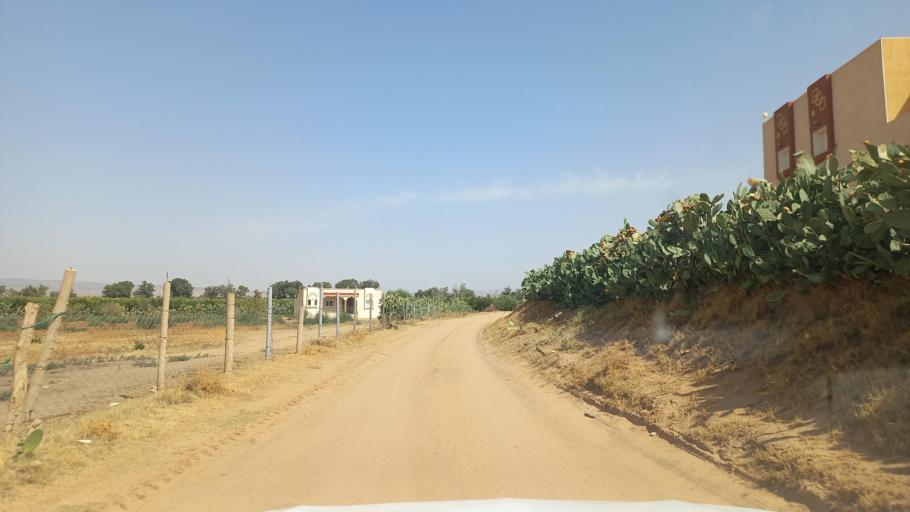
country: TN
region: Al Qasrayn
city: Kasserine
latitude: 35.2564
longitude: 9.0438
